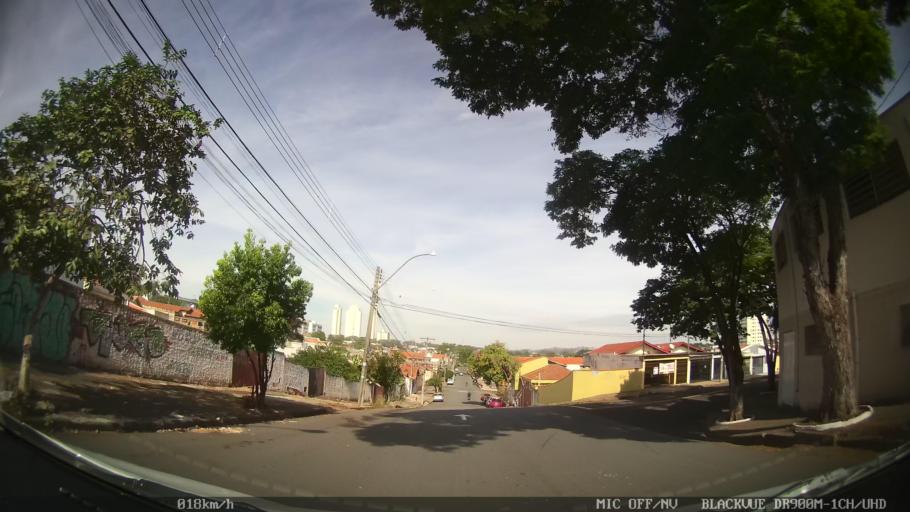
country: BR
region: Sao Paulo
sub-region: Piracicaba
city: Piracicaba
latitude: -22.7084
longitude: -47.6581
